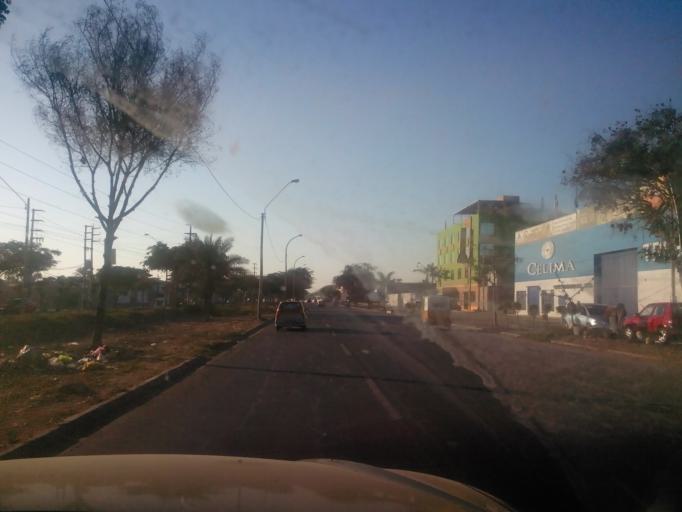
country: PE
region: Ica
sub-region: Provincia de Ica
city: Ica
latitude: -14.0625
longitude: -75.7411
